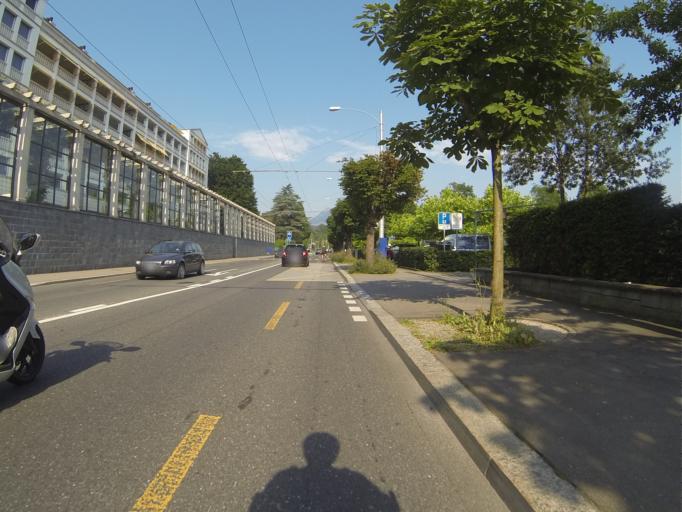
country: CH
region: Lucerne
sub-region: Lucerne-Stadt District
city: Luzern
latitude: 47.0555
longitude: 8.3233
